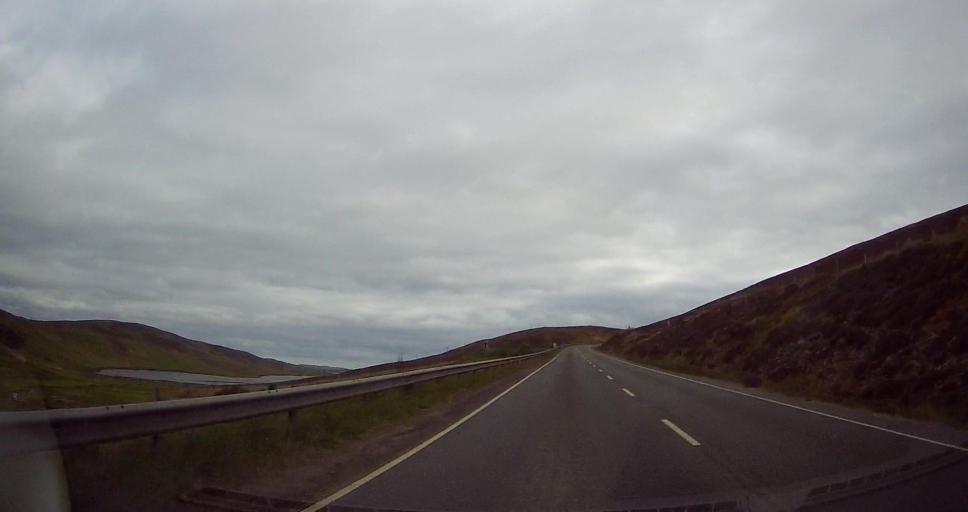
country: GB
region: Scotland
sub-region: Shetland Islands
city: Lerwick
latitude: 60.1625
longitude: -1.2196
